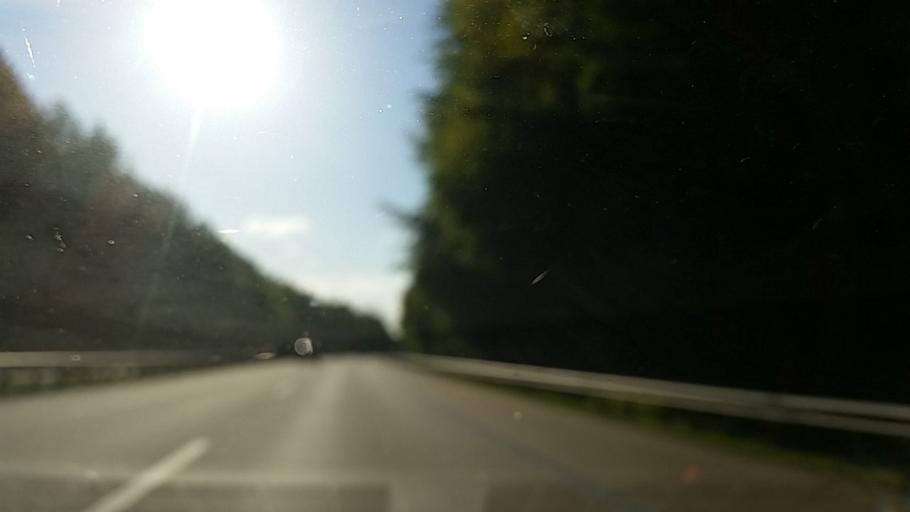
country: DE
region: Schleswig-Holstein
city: Witzhave
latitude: 53.5608
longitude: 10.3483
